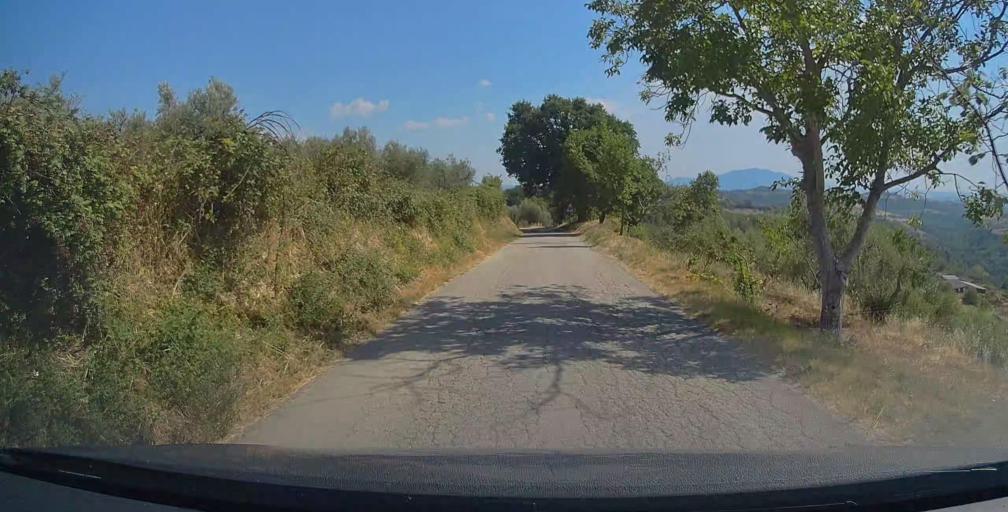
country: IT
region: Umbria
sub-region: Provincia di Terni
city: Calvi dell'Umbria
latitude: 42.3832
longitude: 12.5685
